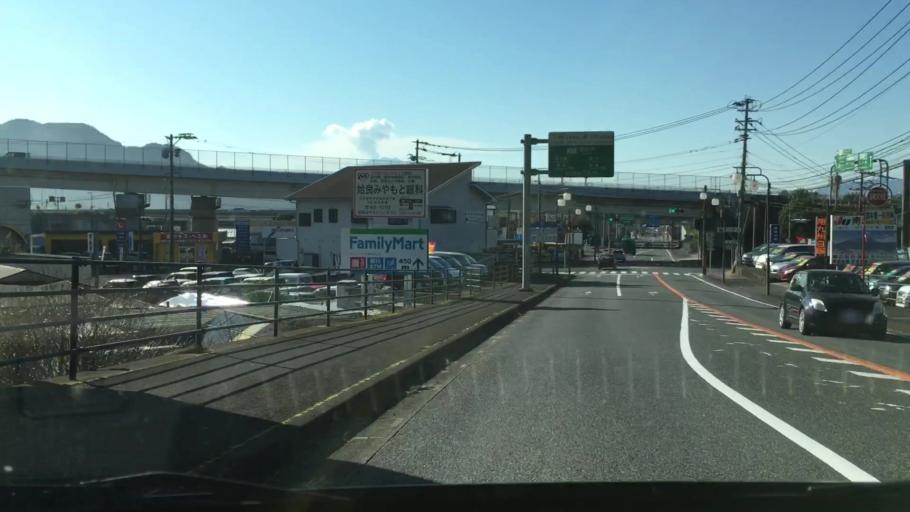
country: JP
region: Kagoshima
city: Kajiki
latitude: 31.7482
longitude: 130.6711
